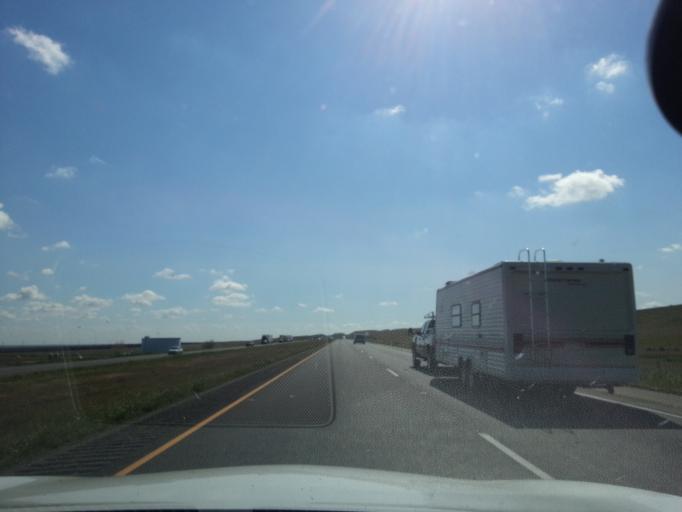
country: US
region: California
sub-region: Fresno County
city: Coalinga
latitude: 36.3431
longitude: -120.3115
